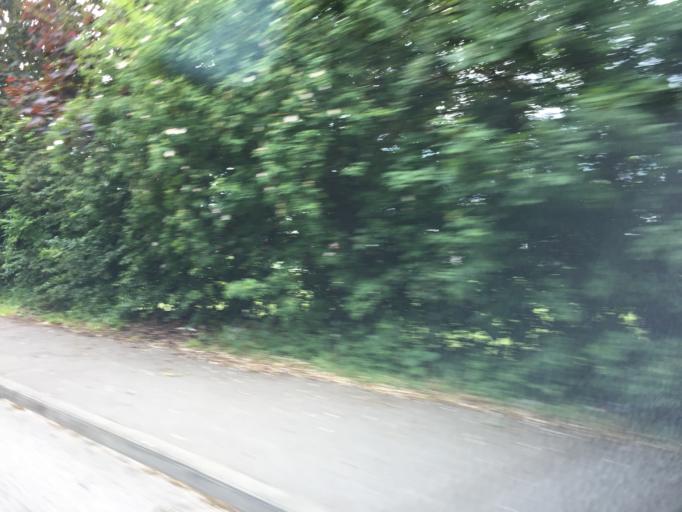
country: GB
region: England
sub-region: Borough of Swindon
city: Broad Blunsdon
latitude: 51.5891
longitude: -1.7569
